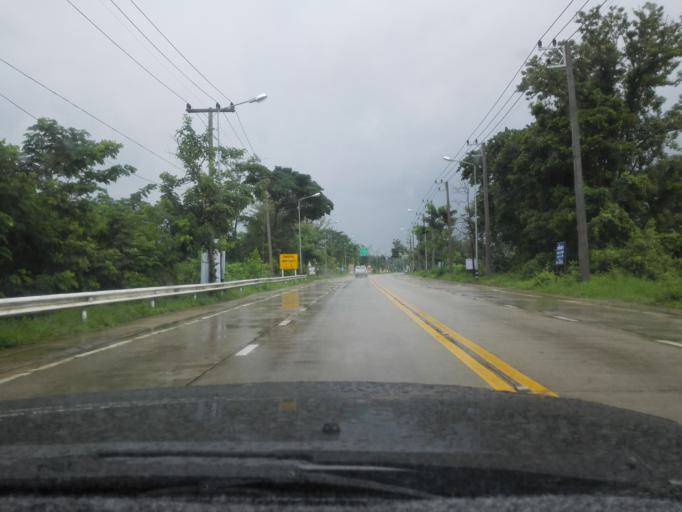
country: TH
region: Tak
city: Mae Sot
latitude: 16.7120
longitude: 98.5787
